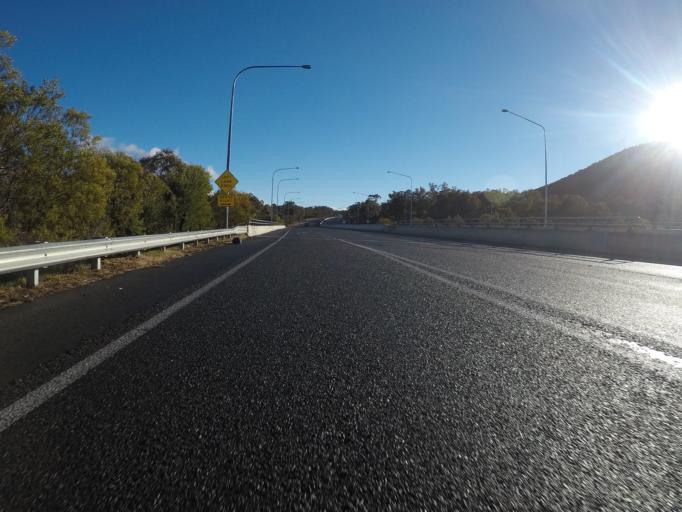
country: AU
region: Australian Capital Territory
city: Acton
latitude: -35.2809
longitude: 149.0862
